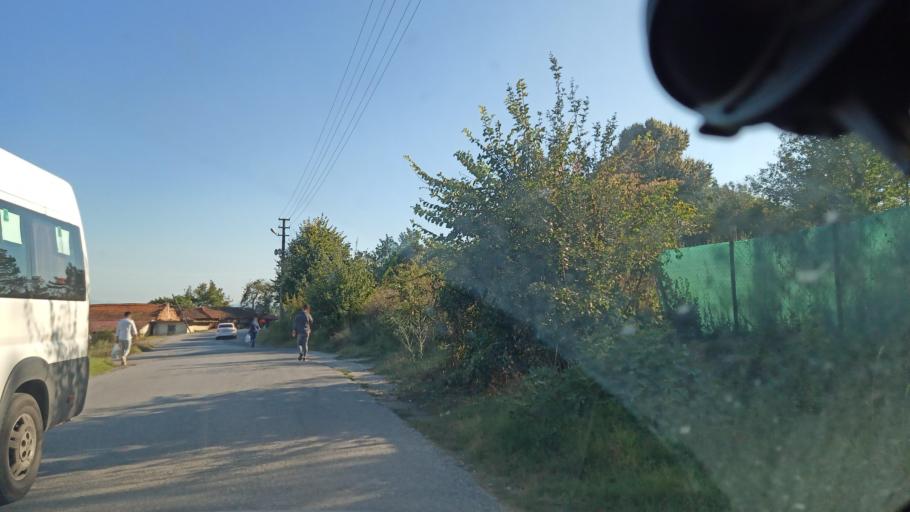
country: TR
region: Sakarya
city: Kazimpasa
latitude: 40.8561
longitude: 30.2850
